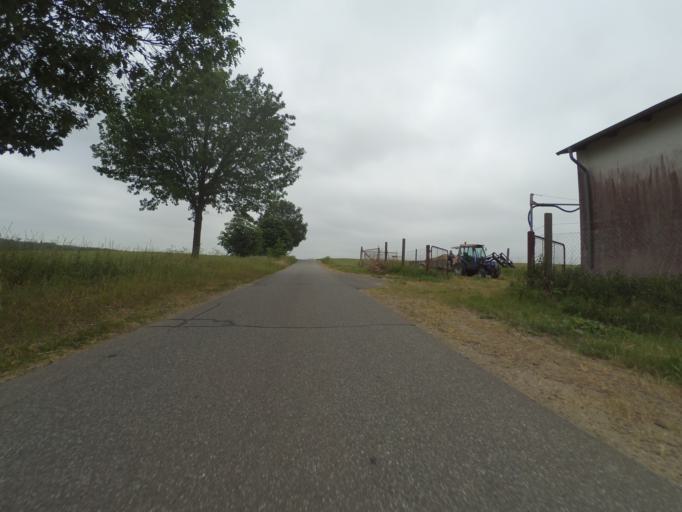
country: DE
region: Mecklenburg-Vorpommern
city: Plau am See
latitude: 53.4969
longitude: 12.2032
